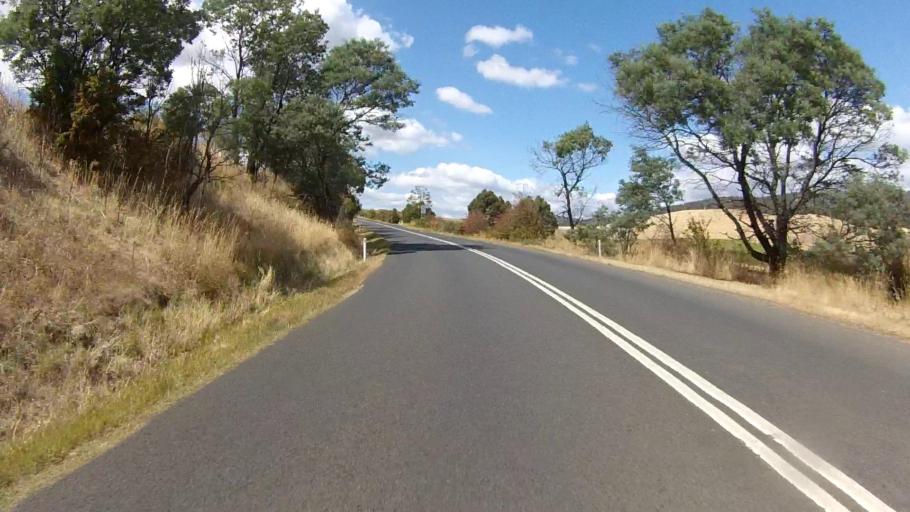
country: AU
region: Tasmania
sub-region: Derwent Valley
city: New Norfolk
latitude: -42.7358
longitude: 146.9287
